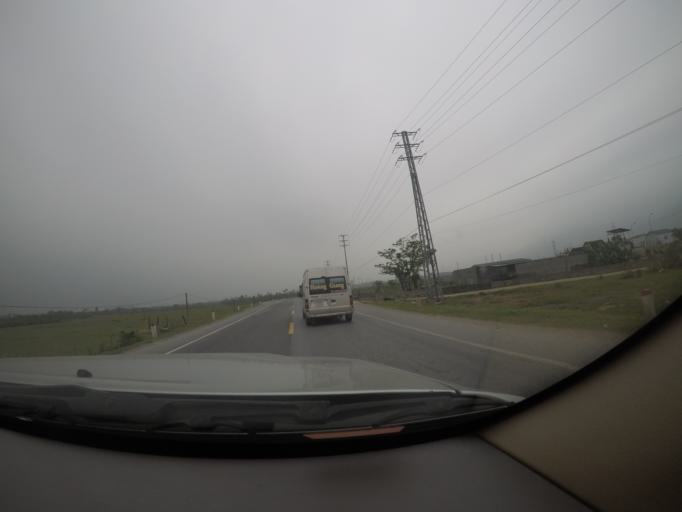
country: VN
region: Ha Tinh
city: Ky Anh
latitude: 18.0206
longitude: 106.3811
